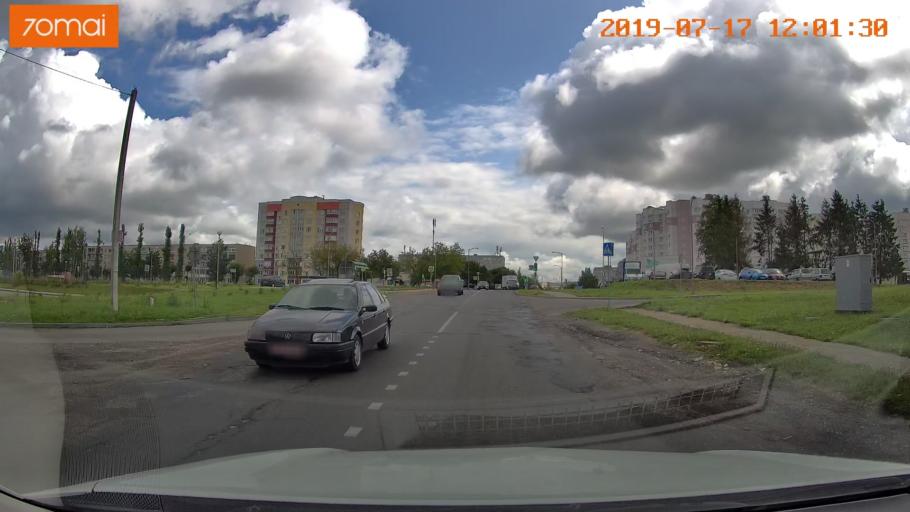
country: BY
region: Minsk
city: Borovlyany
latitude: 54.0048
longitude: 27.6763
